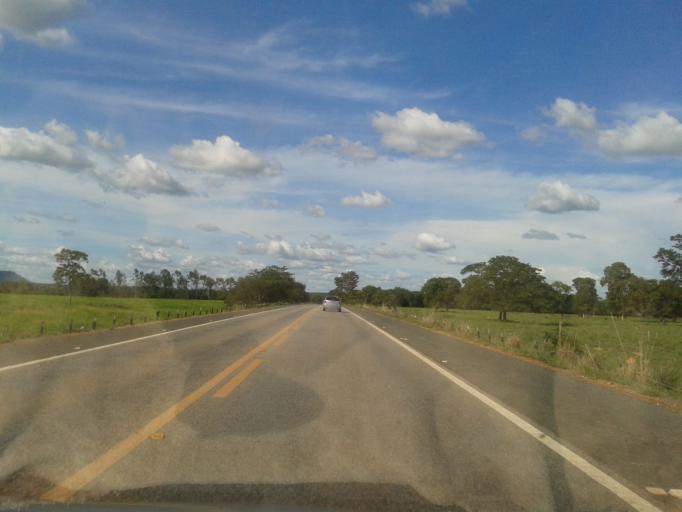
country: BR
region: Goias
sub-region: Mozarlandia
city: Mozarlandia
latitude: -15.0119
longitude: -50.5936
